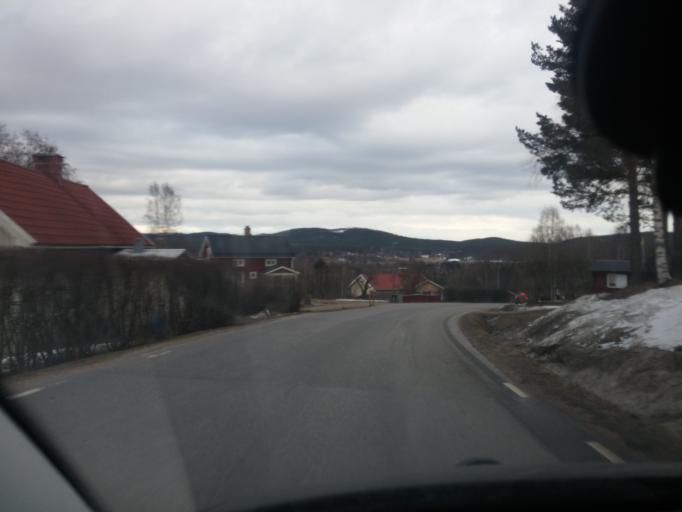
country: SE
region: Gaevleborg
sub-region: Ljusdals Kommun
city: Jaervsoe
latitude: 61.7244
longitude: 16.1637
